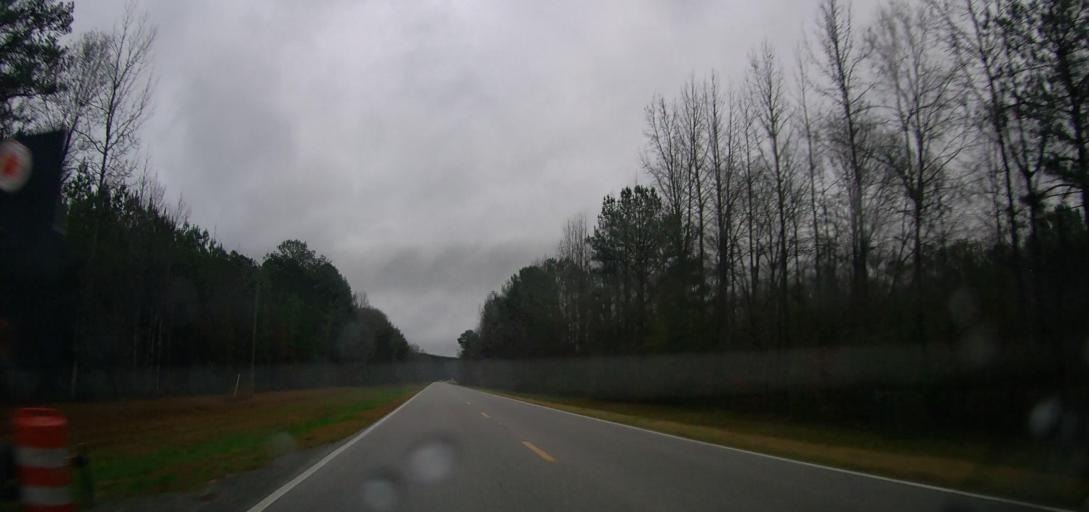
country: US
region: Alabama
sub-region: Bibb County
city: Centreville
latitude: 32.9232
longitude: -87.0389
